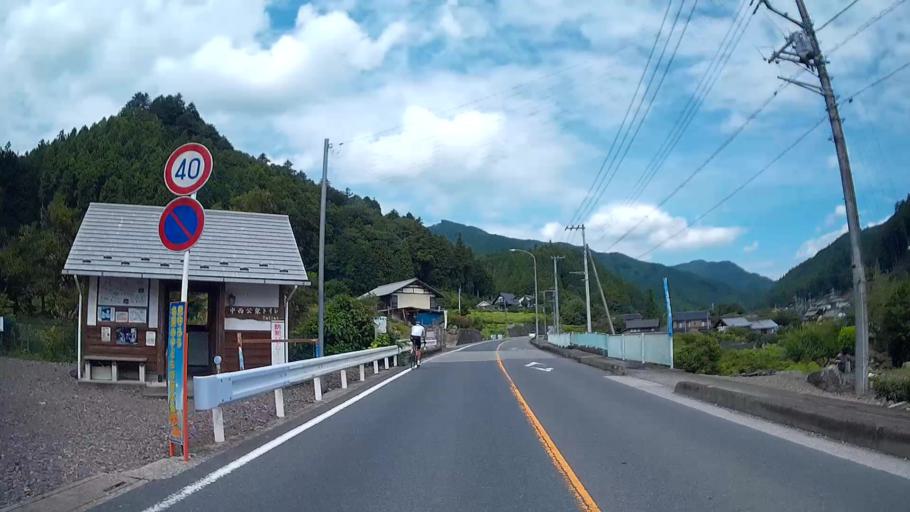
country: JP
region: Tokyo
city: Ome
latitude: 35.8542
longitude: 139.1946
